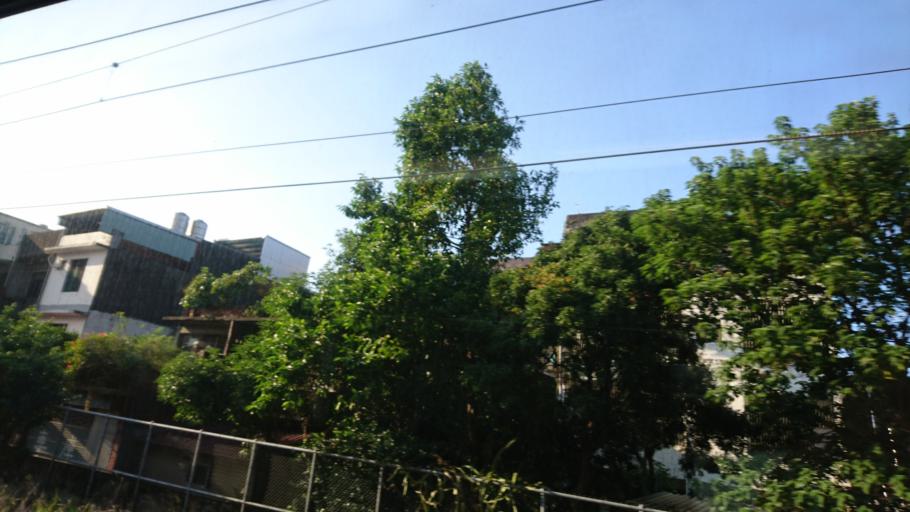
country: TW
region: Taiwan
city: Taoyuan City
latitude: 24.9564
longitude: 121.2329
